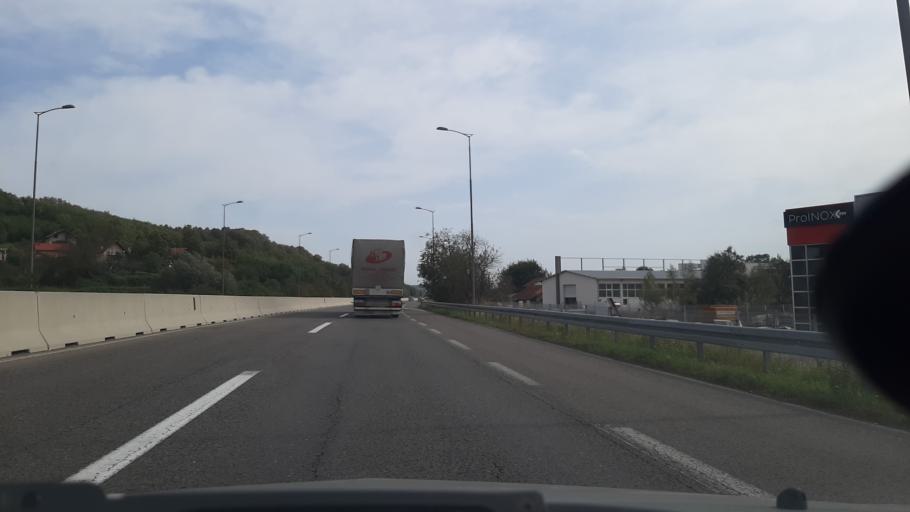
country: BA
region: Republika Srpska
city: Trn
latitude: 44.8717
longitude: 17.2615
